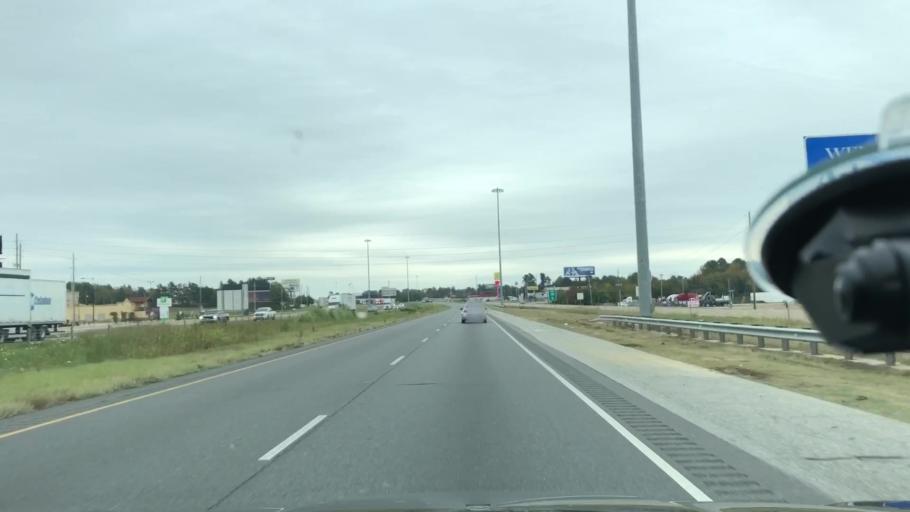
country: US
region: Arkansas
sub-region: Miller County
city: Texarkana
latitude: 33.4701
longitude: -94.0392
